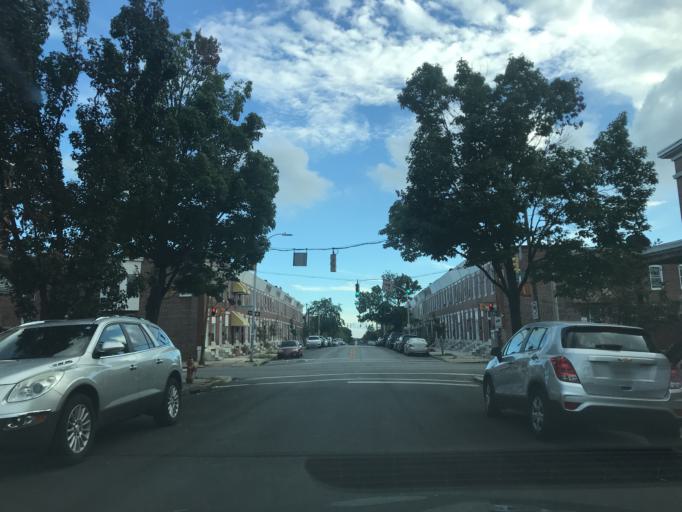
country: US
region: Maryland
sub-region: City of Baltimore
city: Baltimore
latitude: 39.3005
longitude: -76.5768
